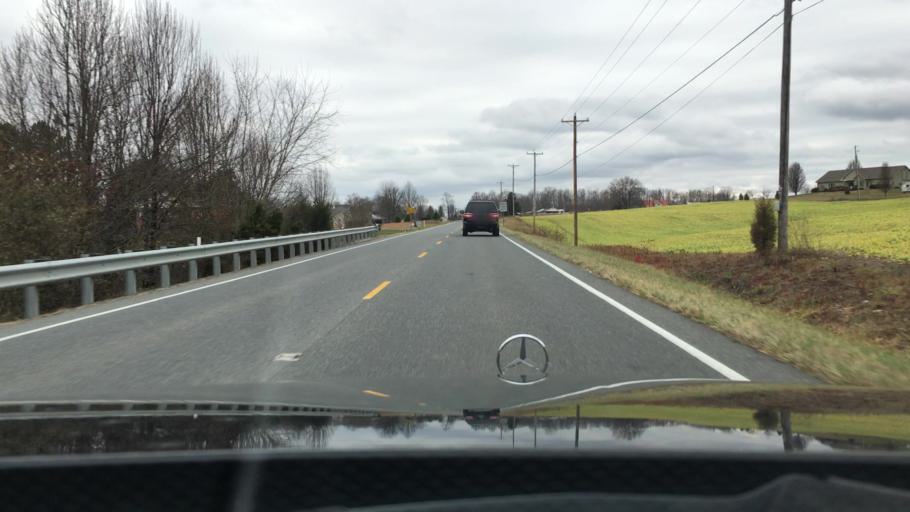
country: US
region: Virginia
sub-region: Botetourt County
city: Blue Ridge
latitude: 37.2501
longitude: -79.6943
